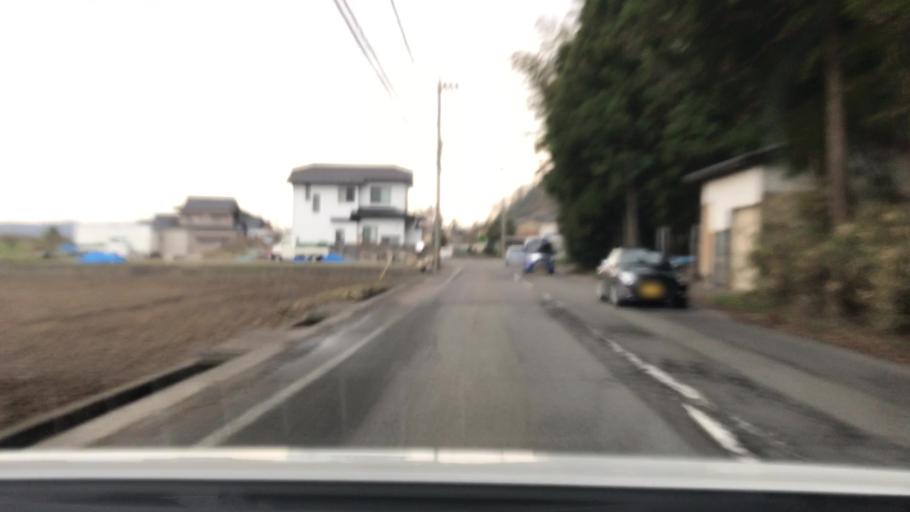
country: JP
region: Fukui
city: Fukui-shi
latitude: 36.0877
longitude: 136.1798
